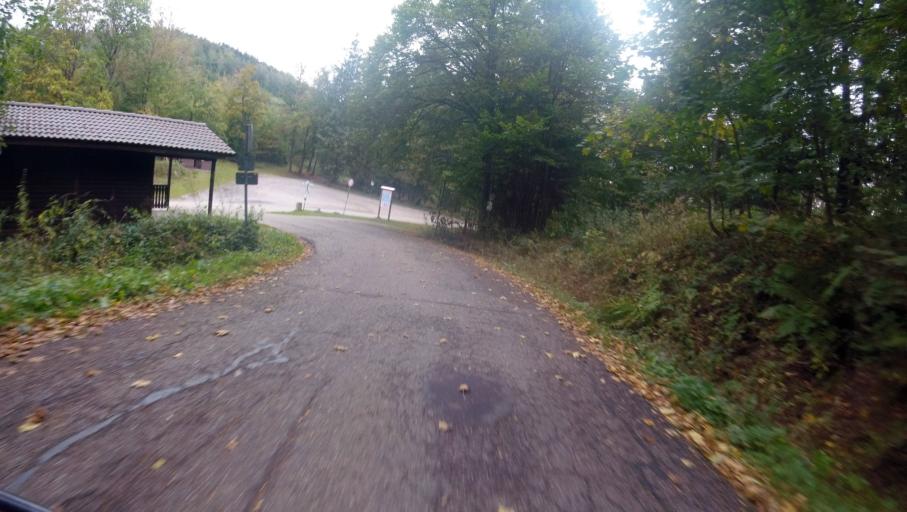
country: DE
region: Baden-Wuerttemberg
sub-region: Karlsruhe Region
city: Bad Herrenalb
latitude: 48.7732
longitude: 8.4165
